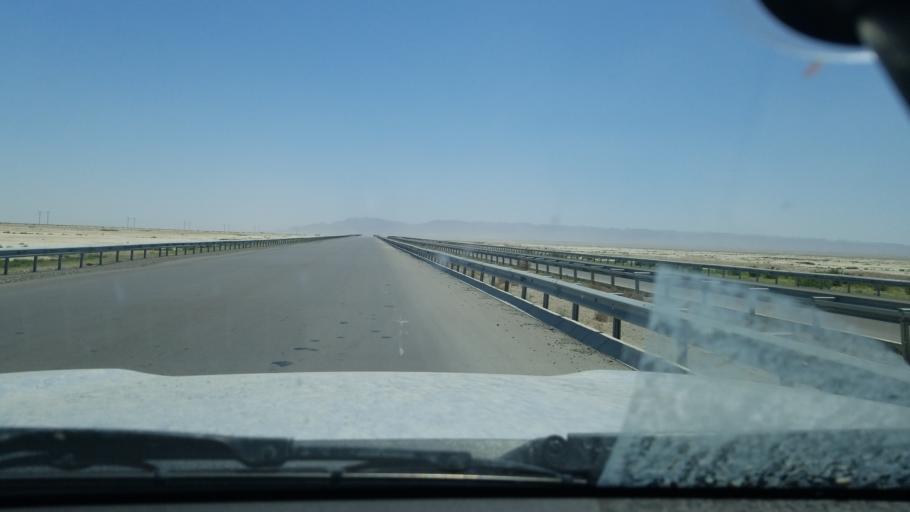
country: TM
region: Balkan
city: Gazanjyk
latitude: 39.2814
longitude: 55.2450
